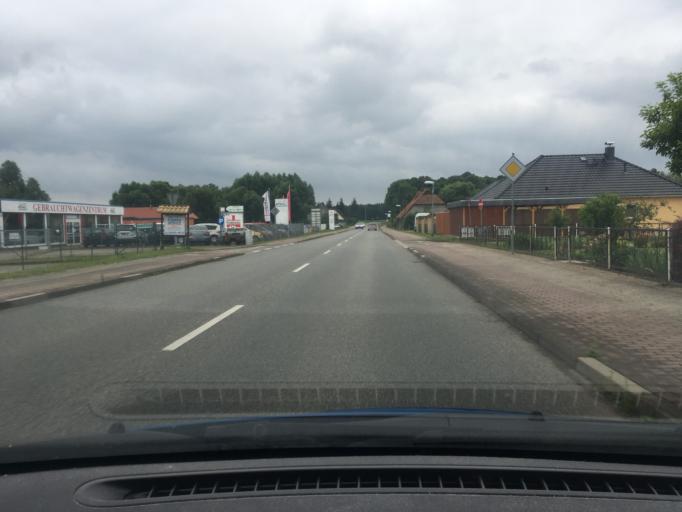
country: DE
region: Mecklenburg-Vorpommern
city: Stralendorf
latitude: 53.5291
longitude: 11.3028
